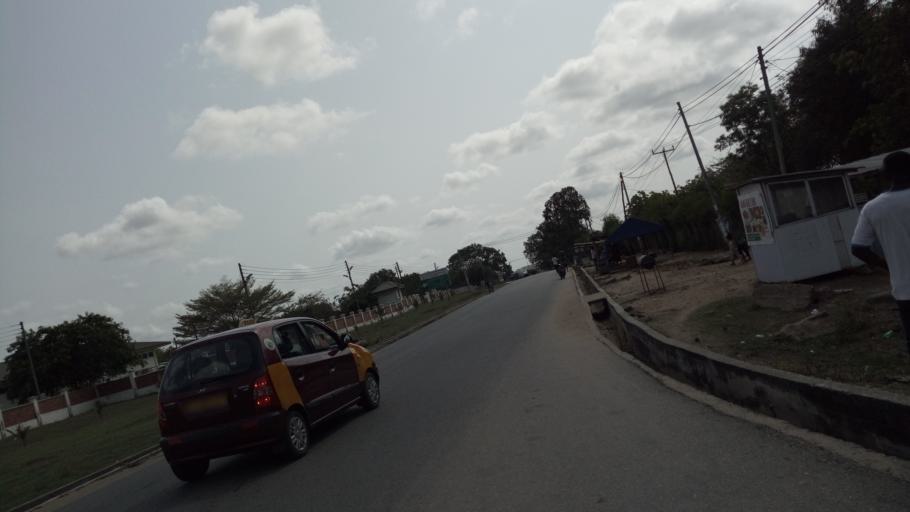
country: GH
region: Central
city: Winneba
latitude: 5.3708
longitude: -0.6416
